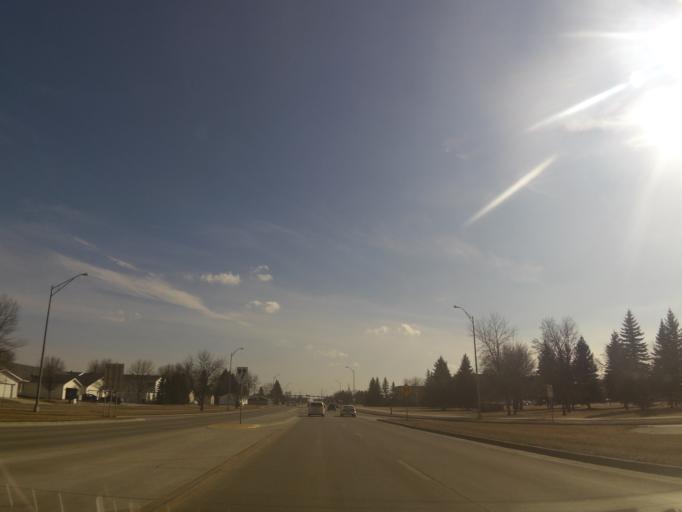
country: US
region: North Dakota
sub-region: Grand Forks County
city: Grand Forks
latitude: 47.9145
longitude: -97.0665
